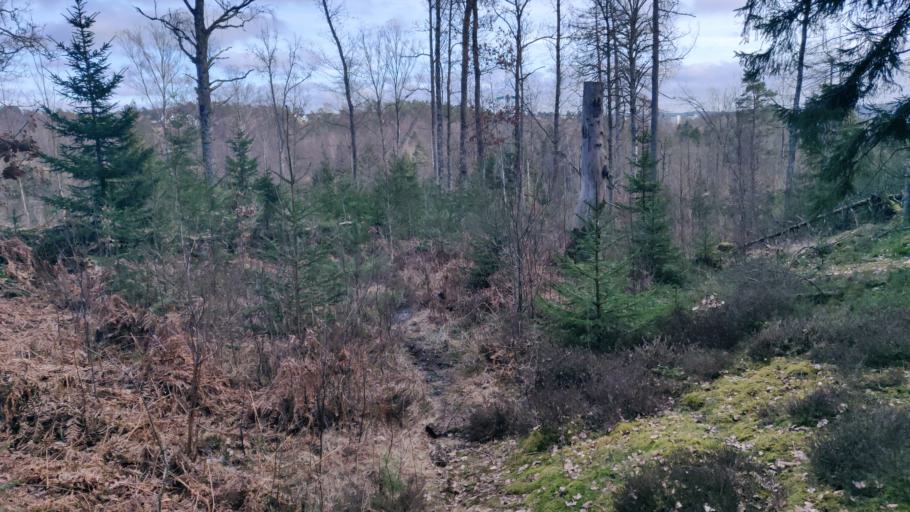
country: SE
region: Vaestra Goetaland
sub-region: Uddevalla Kommun
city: Uddevalla
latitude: 58.3694
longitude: 11.8964
